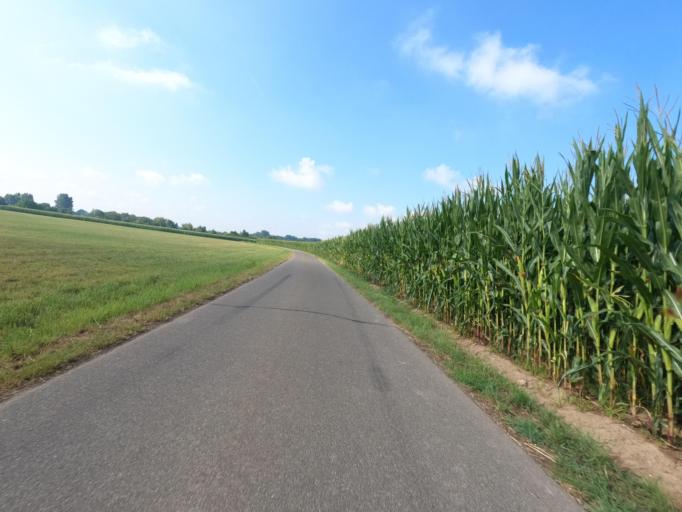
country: DE
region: North Rhine-Westphalia
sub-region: Regierungsbezirk Koln
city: Heinsberg
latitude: 51.0864
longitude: 6.0925
